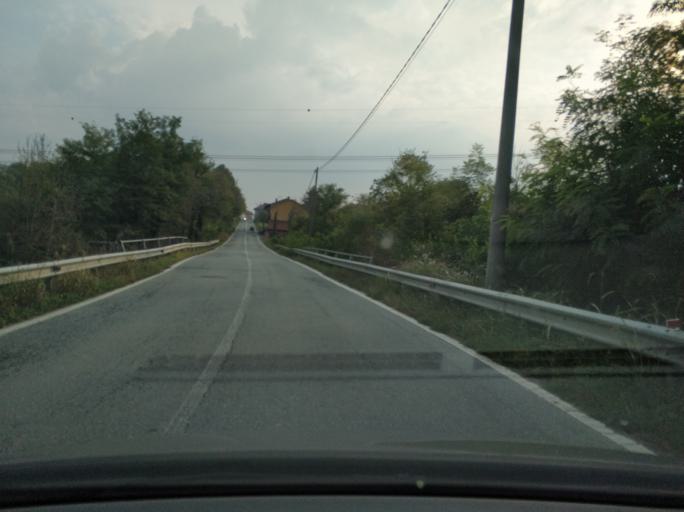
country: IT
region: Piedmont
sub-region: Provincia di Torino
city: San Francesco al Campo
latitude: 45.2412
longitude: 7.6544
